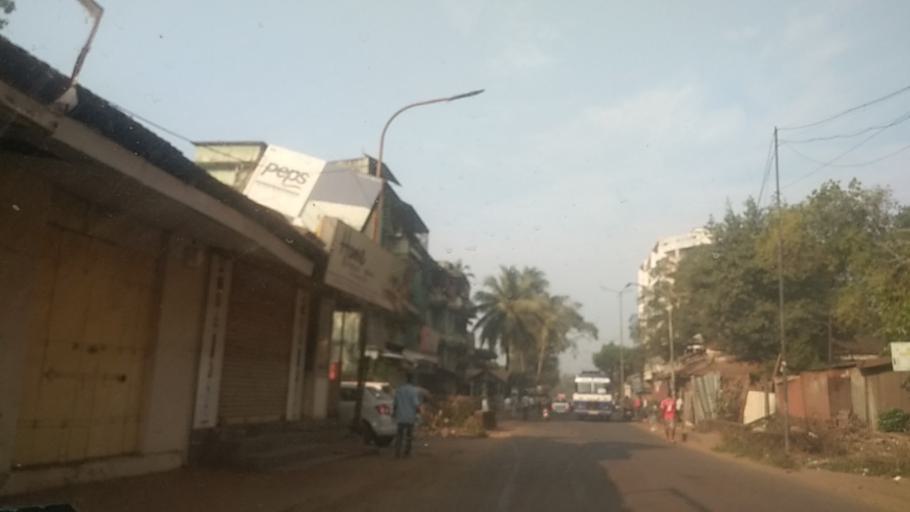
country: IN
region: Goa
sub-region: South Goa
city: Madgaon
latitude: 15.2692
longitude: 73.9558
